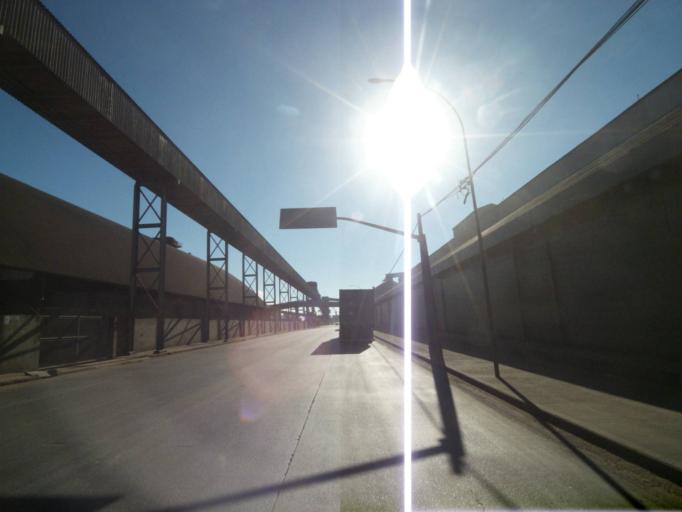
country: BR
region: Parana
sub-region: Paranagua
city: Paranagua
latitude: -25.5091
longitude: -48.5181
